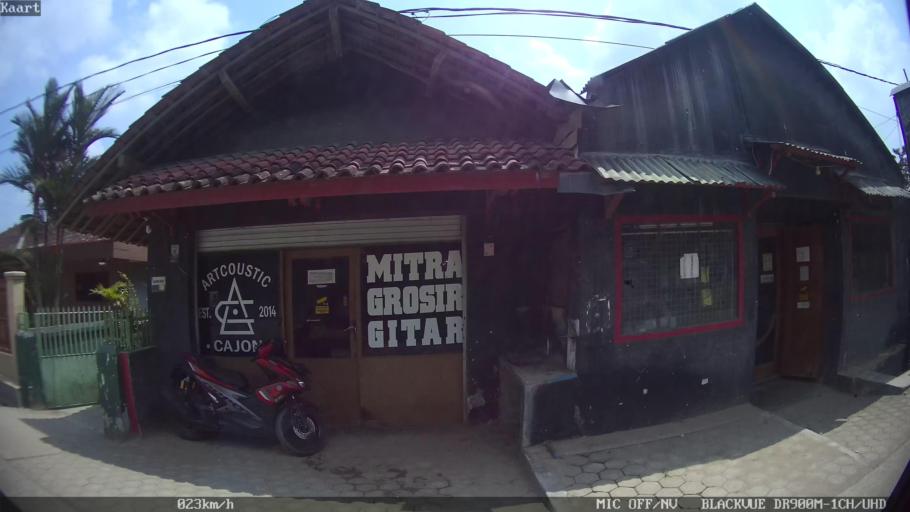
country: ID
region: Lampung
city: Pringsewu
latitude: -5.3620
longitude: 104.9797
